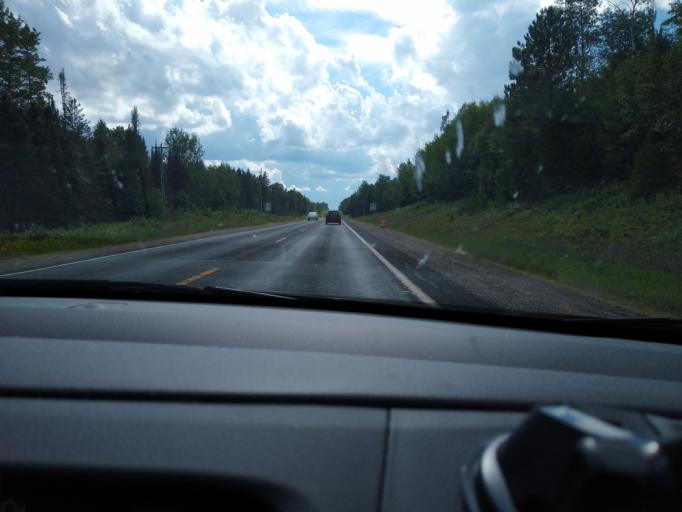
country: US
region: Michigan
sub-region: Marquette County
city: West Ishpeming
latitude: 46.3086
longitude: -87.9808
